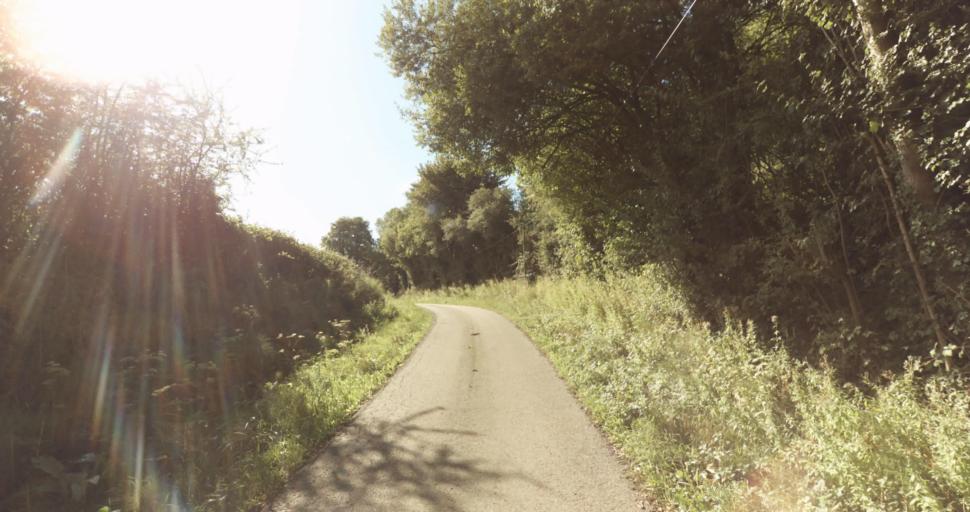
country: FR
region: Lower Normandy
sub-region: Departement de l'Orne
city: Gace
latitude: 48.8128
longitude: 0.2150
